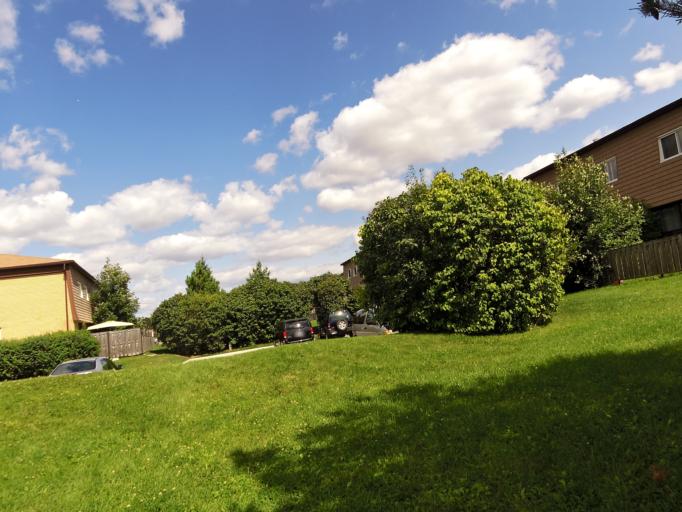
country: CA
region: Ontario
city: Bells Corners
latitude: 45.3480
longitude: -75.8119
